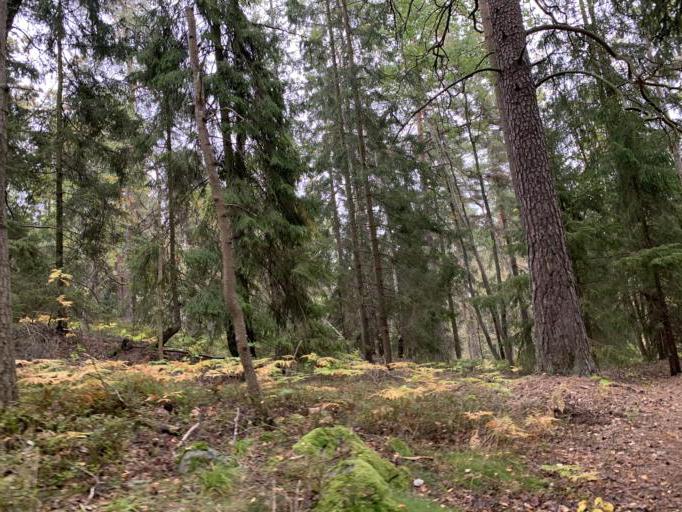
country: SE
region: Stockholm
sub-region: Lidingo
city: Brevik
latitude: 59.3597
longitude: 18.1676
